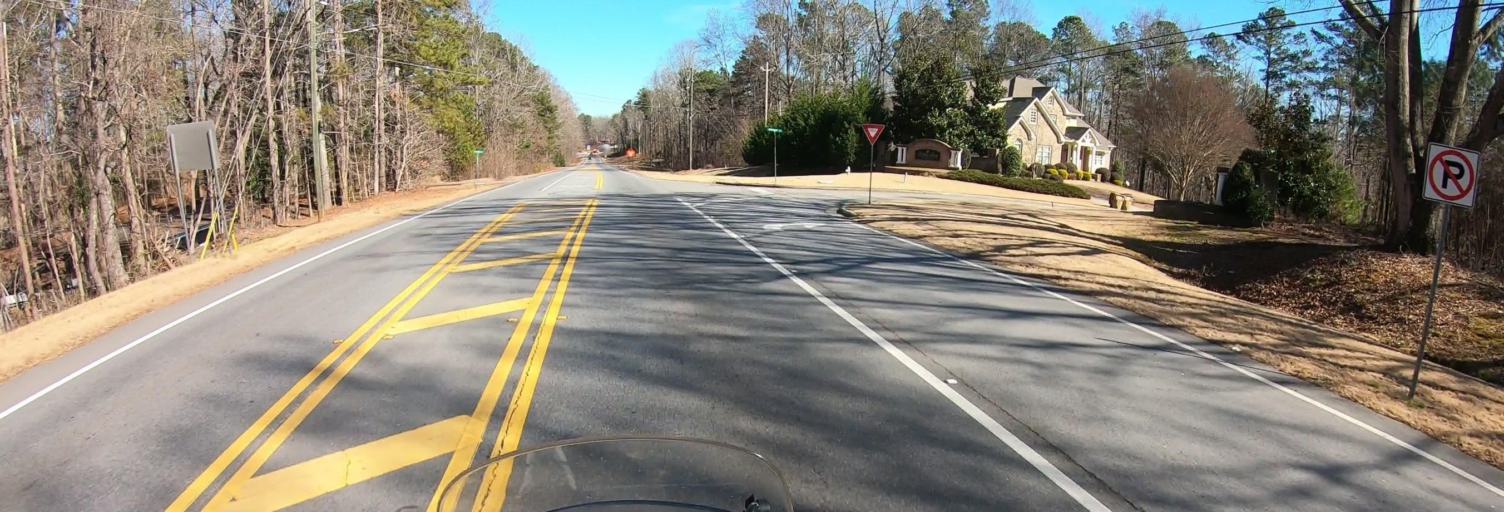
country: US
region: Georgia
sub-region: Hall County
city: Flowery Branch
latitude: 34.2566
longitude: -83.9646
